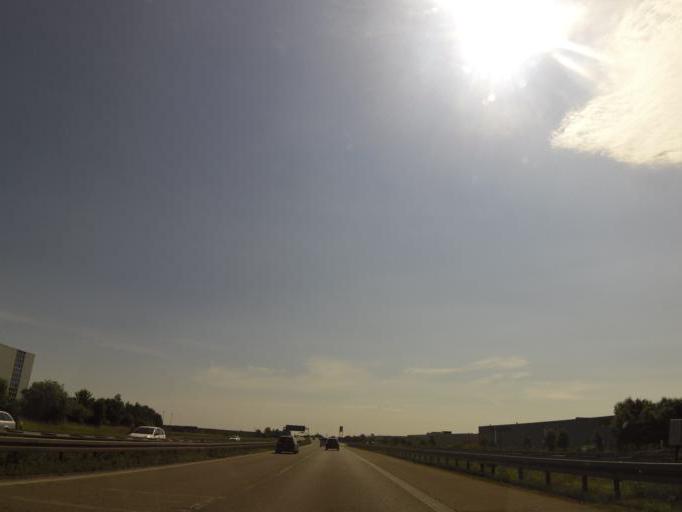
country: DE
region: Baden-Wuerttemberg
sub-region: Tuebingen Region
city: Dornstadt
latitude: 48.4560
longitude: 9.9654
